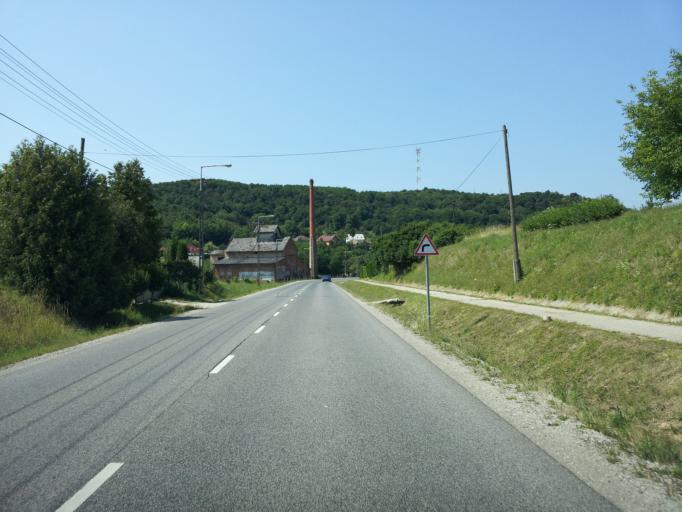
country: HU
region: Zala
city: Pacsa
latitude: 46.8187
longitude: 17.0028
